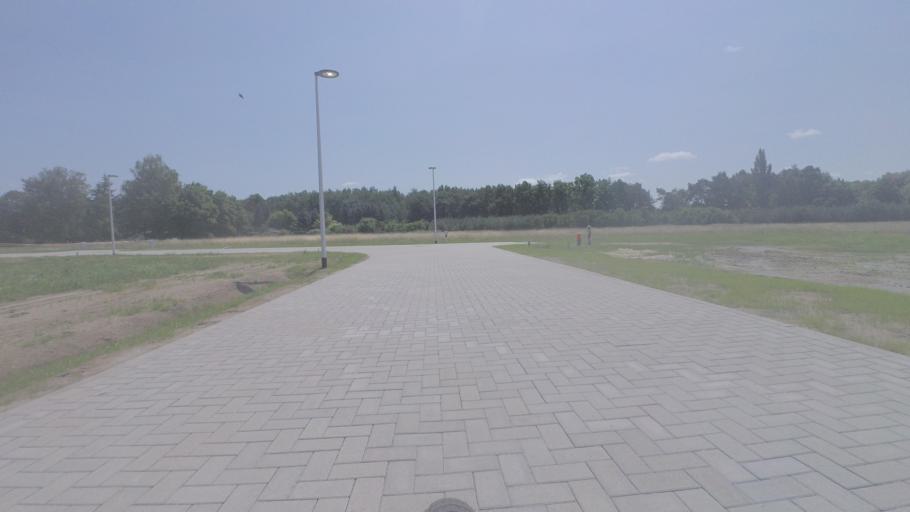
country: DE
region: Brandenburg
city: Zossen
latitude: 52.2448
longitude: 13.4201
